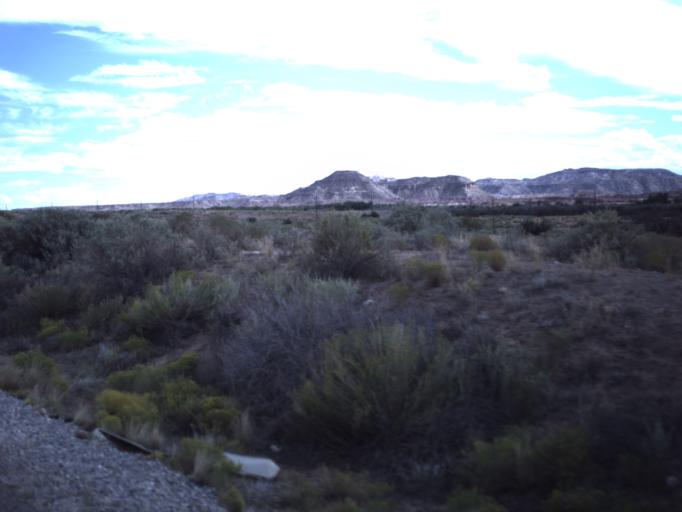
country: US
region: Utah
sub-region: San Juan County
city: Blanding
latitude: 37.2339
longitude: -109.2205
